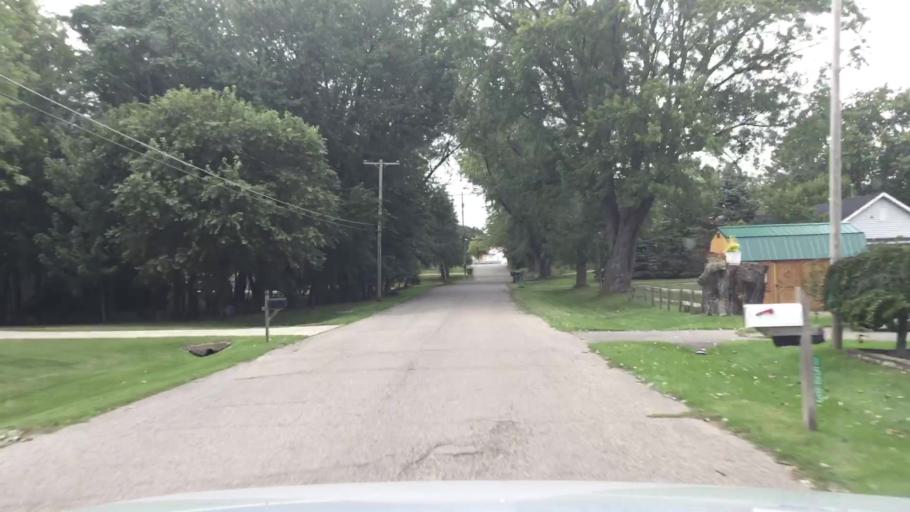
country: US
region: Michigan
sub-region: Genesee County
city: Linden
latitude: 42.8091
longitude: -83.7994
